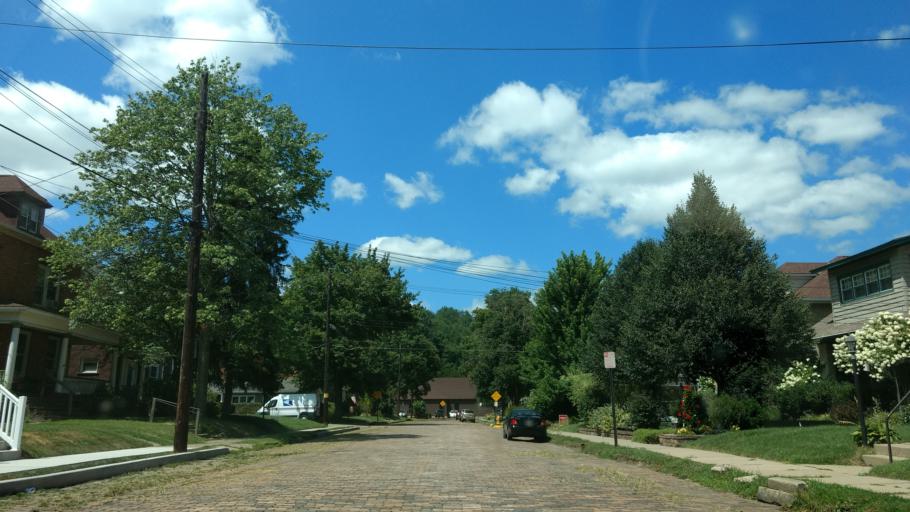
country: US
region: Pennsylvania
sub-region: Beaver County
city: Beaver
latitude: 40.7003
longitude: -80.3003
